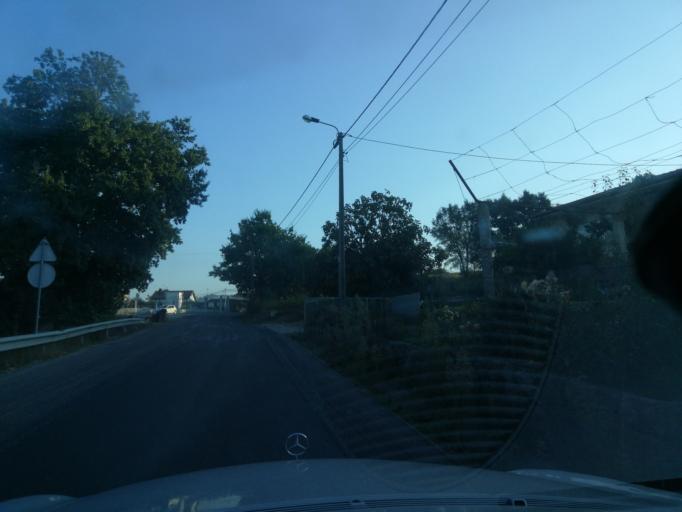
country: PT
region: Braga
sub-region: Braga
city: Braga
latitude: 41.5221
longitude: -8.4323
